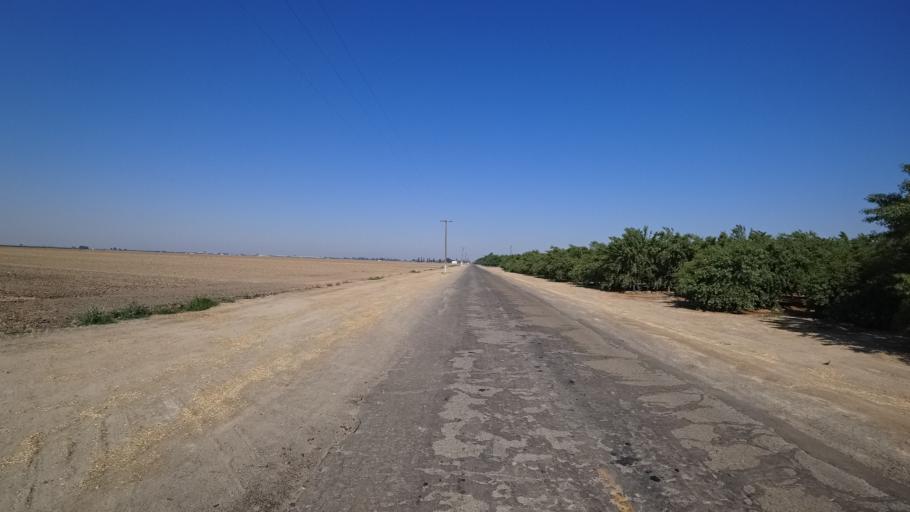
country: US
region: California
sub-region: Fresno County
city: Kingsburg
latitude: 36.4160
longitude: -119.5403
